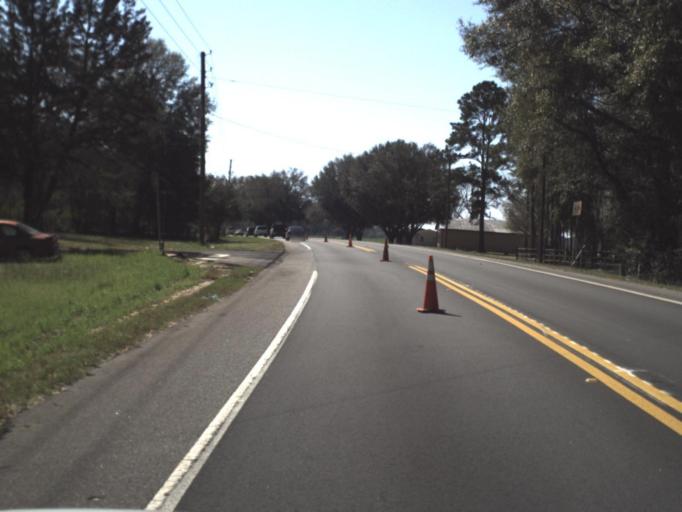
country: US
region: Florida
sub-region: Jackson County
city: Marianna
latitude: 30.7040
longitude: -85.1851
